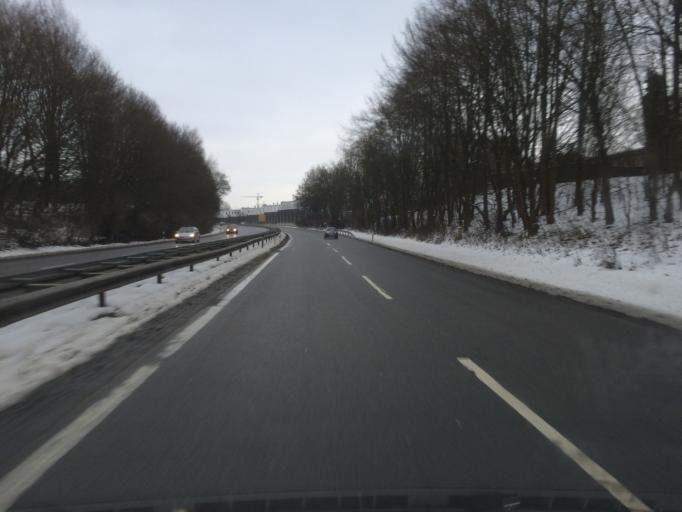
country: DE
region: Bavaria
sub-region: Upper Palatinate
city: Pentling
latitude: 49.0018
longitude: 12.0721
